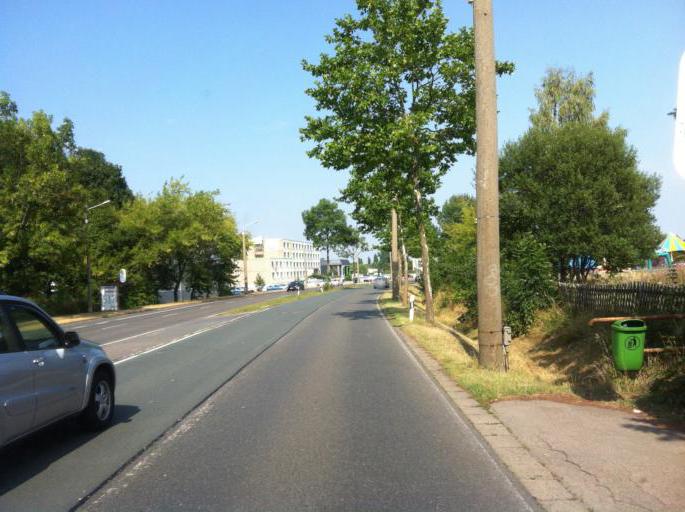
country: DE
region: Saxony
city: Lichtentanne
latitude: 50.7040
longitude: 12.4509
